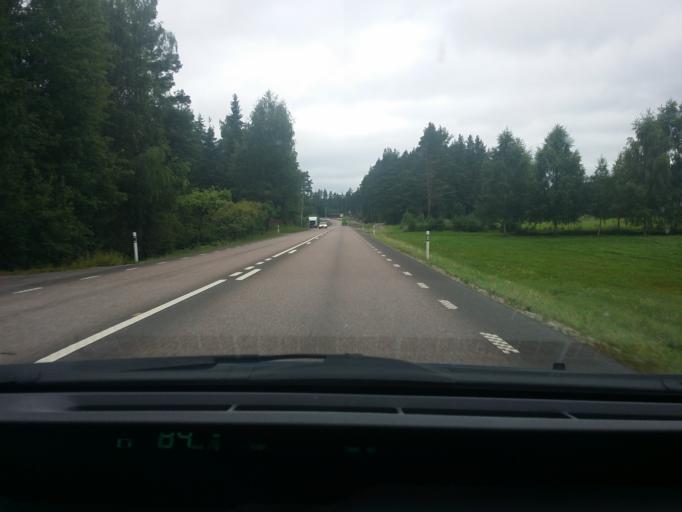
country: SE
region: Dalarna
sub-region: Borlange Kommun
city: Borlaenge
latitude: 60.5252
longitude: 15.3526
